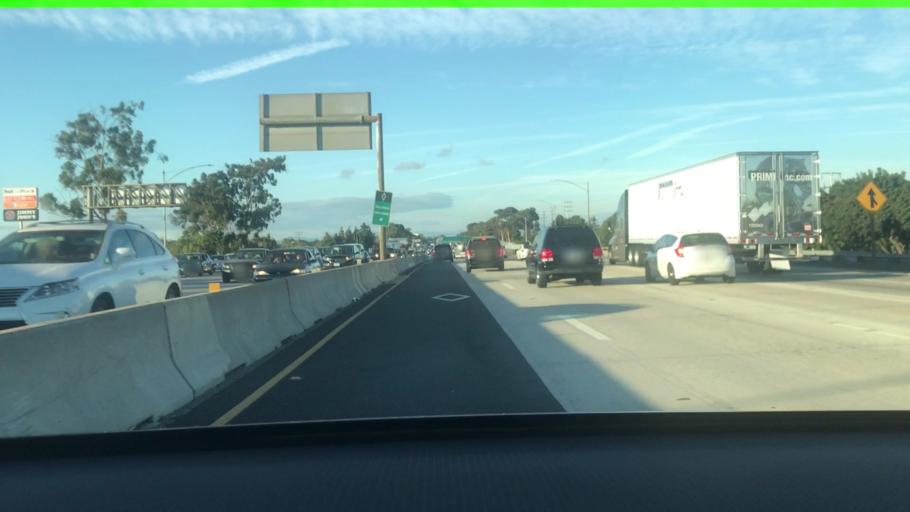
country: US
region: California
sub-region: Los Angeles County
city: Del Aire
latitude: 33.9009
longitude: -118.3705
